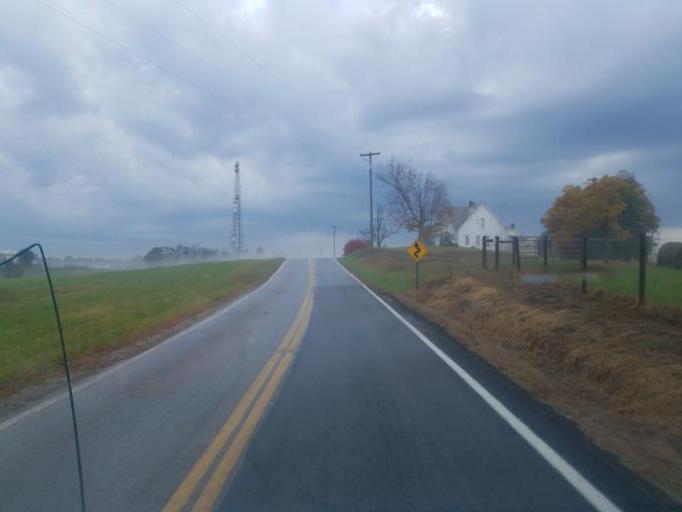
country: US
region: Ohio
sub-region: Morgan County
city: McConnelsville
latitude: 39.4921
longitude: -81.8822
